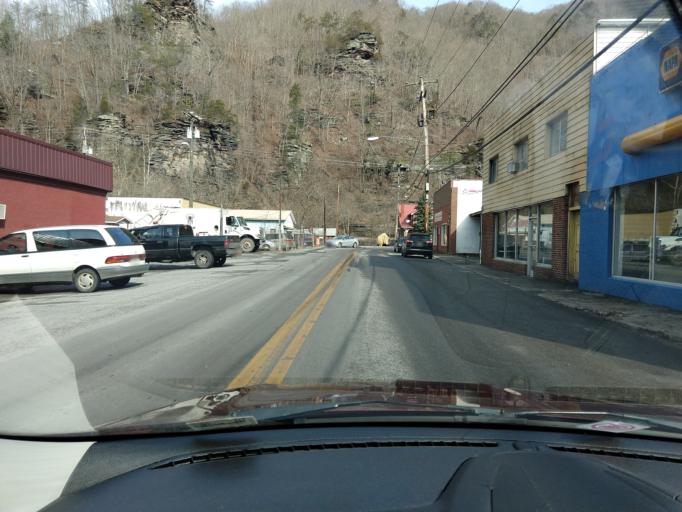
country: US
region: West Virginia
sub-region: McDowell County
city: Welch
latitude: 37.3513
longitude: -81.7985
